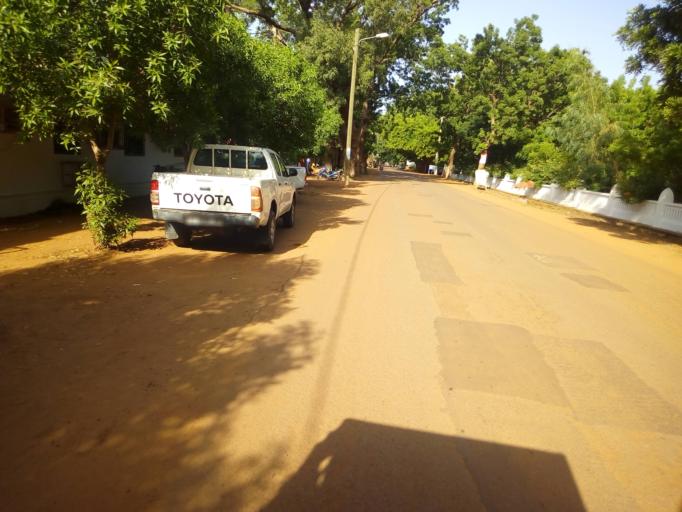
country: ML
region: Segou
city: Segou
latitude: 13.4397
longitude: -6.2799
